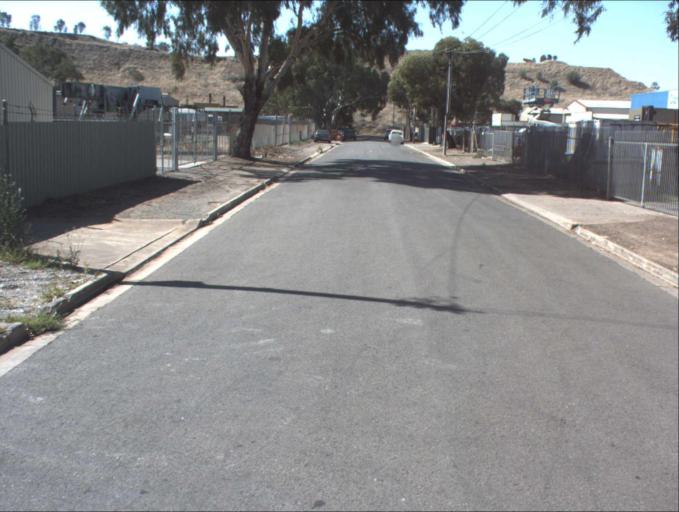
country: AU
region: South Australia
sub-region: Charles Sturt
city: Woodville North
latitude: -34.8363
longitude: 138.5577
